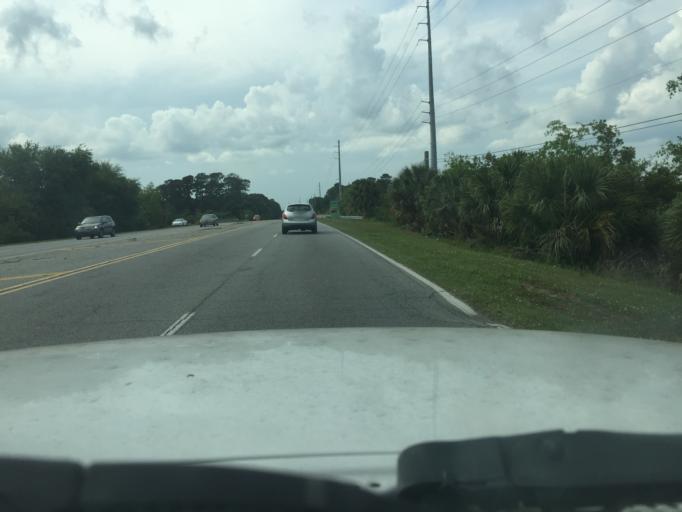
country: US
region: Georgia
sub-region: Chatham County
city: Whitemarsh Island
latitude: 32.0501
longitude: -81.0111
